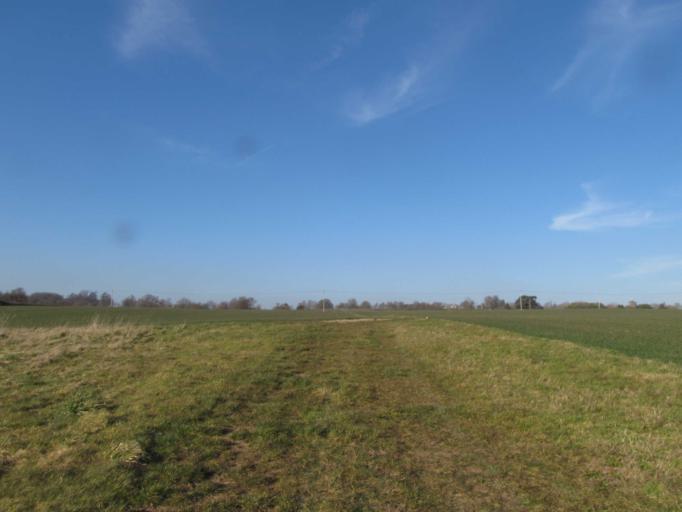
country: GB
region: England
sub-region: West Sussex
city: Petworth
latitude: 50.9799
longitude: -0.6177
